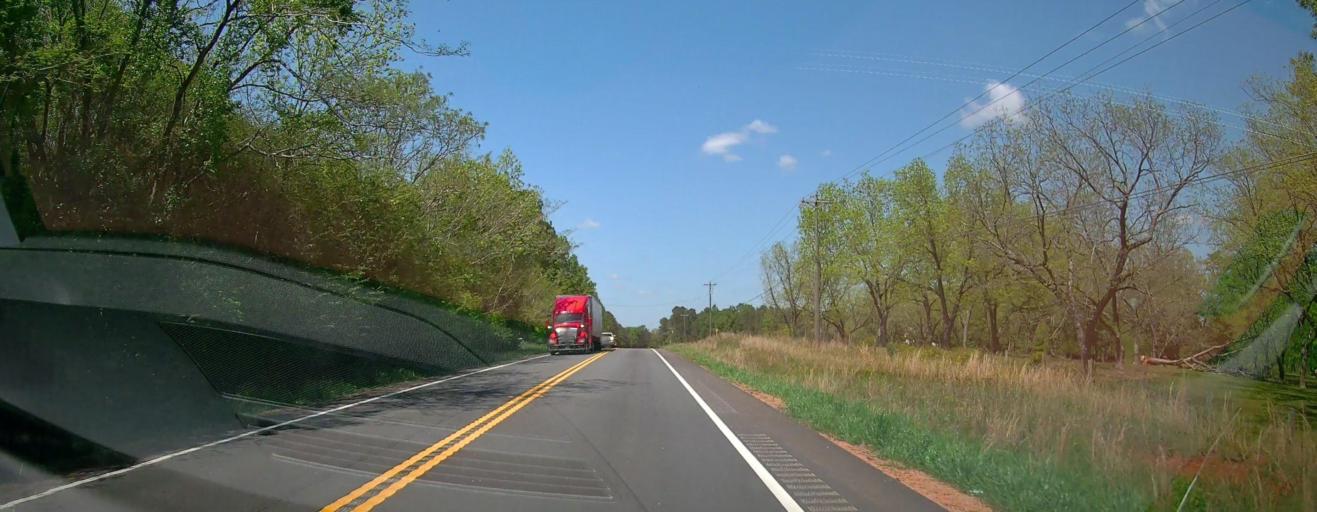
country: US
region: Georgia
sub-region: Putnam County
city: Eatonton
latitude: 33.2040
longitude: -83.4333
